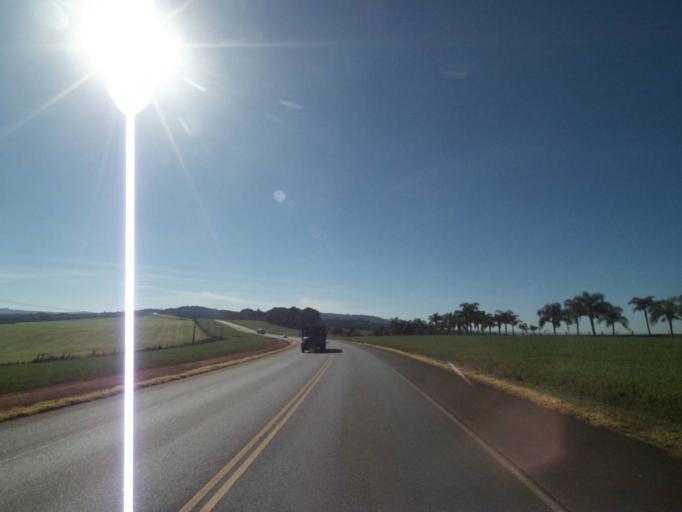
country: BR
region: Parana
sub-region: Tibagi
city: Tibagi
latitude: -24.4232
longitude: -50.3752
